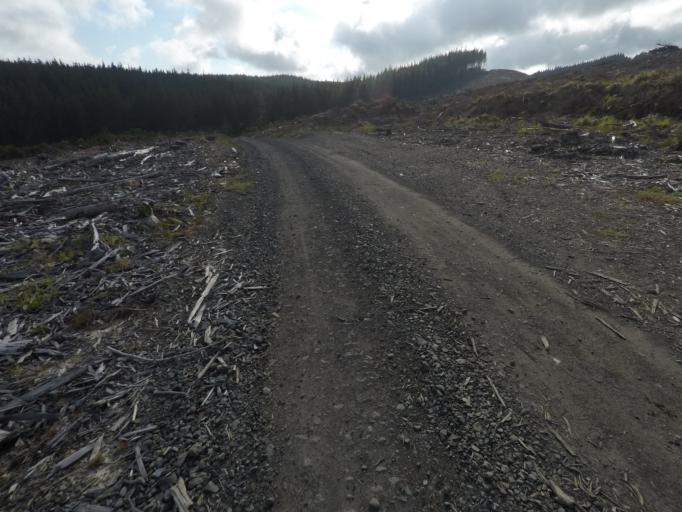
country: NZ
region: Auckland
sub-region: Auckland
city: Parakai
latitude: -36.7128
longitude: 174.5704
